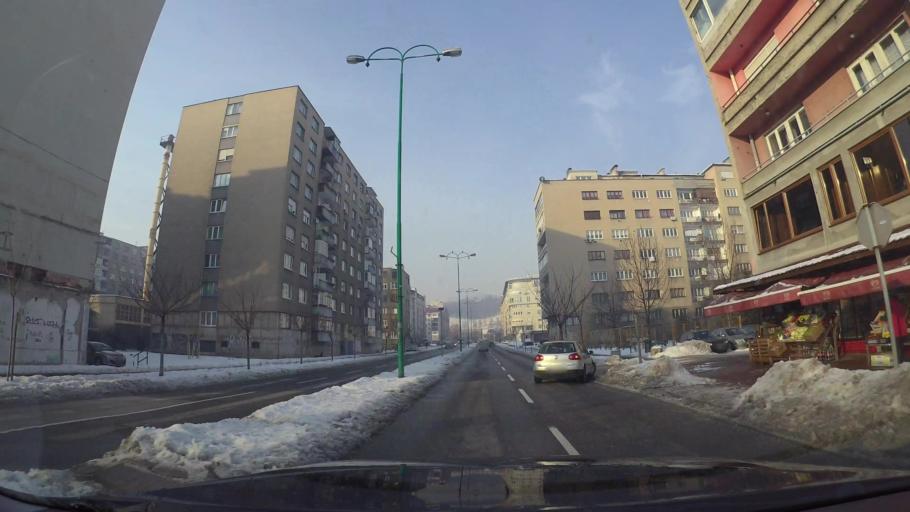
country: BA
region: Federation of Bosnia and Herzegovina
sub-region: Kanton Sarajevo
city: Sarajevo
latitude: 43.8512
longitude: 18.3723
